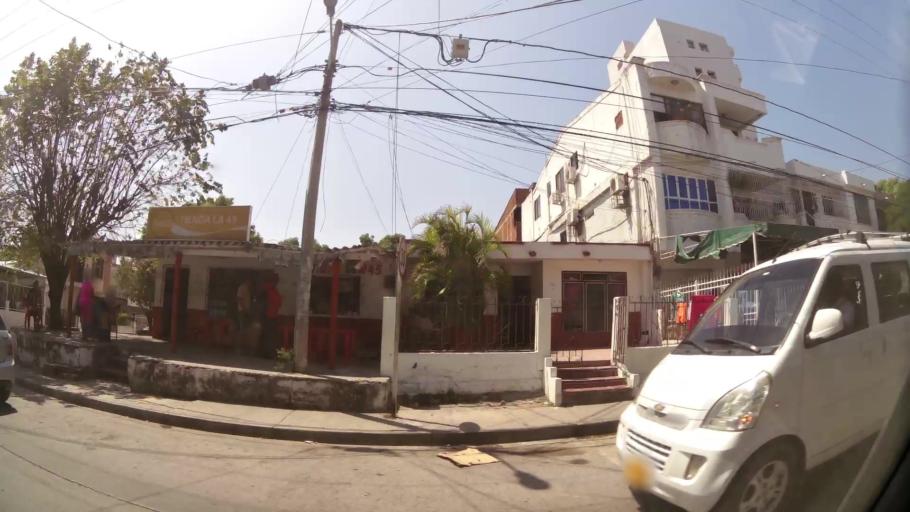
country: CO
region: Bolivar
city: Cartagena
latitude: 10.3987
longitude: -75.4880
